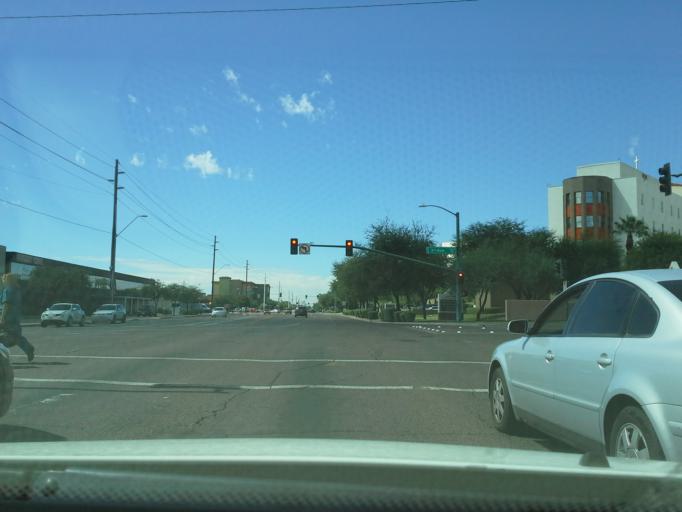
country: US
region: Arizona
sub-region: Maricopa County
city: Phoenix
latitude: 33.4804
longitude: -112.0779
